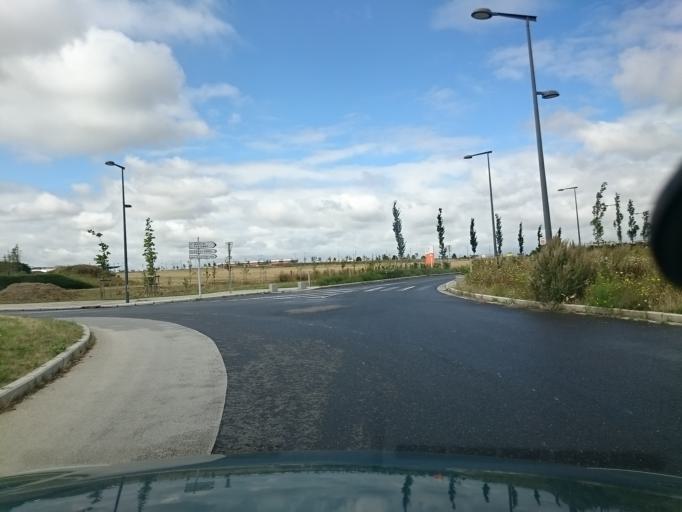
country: FR
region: Lower Normandy
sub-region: Departement du Calvados
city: Fleury-sur-Orne
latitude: 49.1421
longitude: -0.3675
